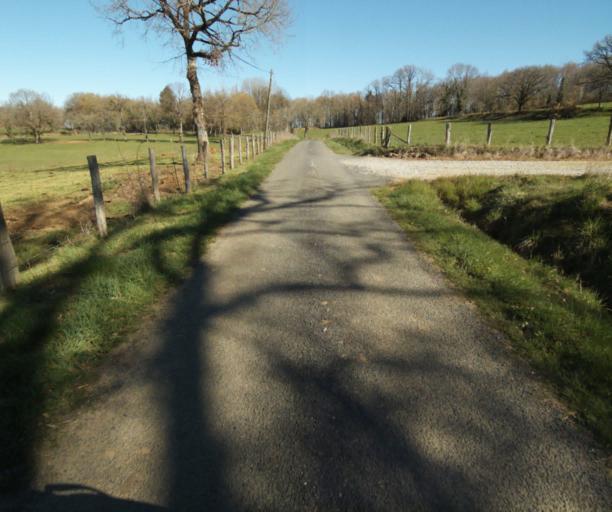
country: FR
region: Limousin
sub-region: Departement de la Correze
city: Chamboulive
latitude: 45.4083
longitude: 1.6877
